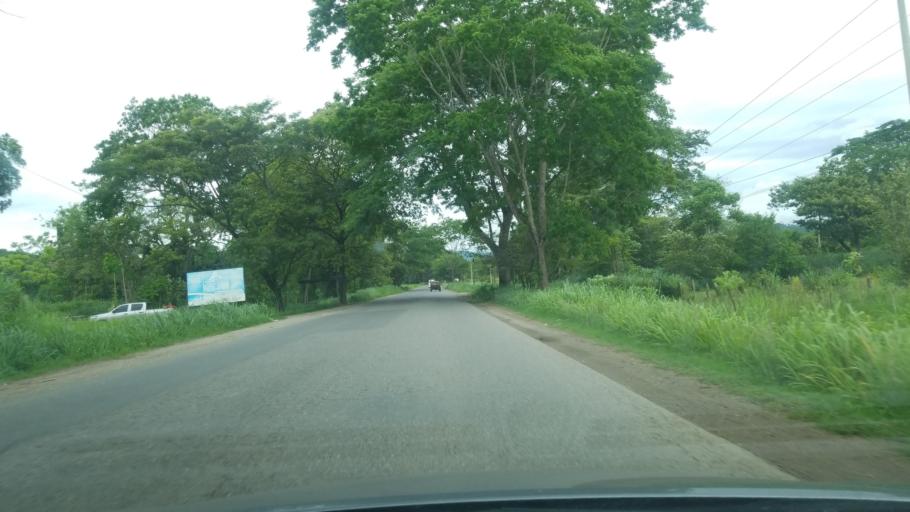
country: HN
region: Santa Barbara
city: La Flecha
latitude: 15.2967
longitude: -88.4658
